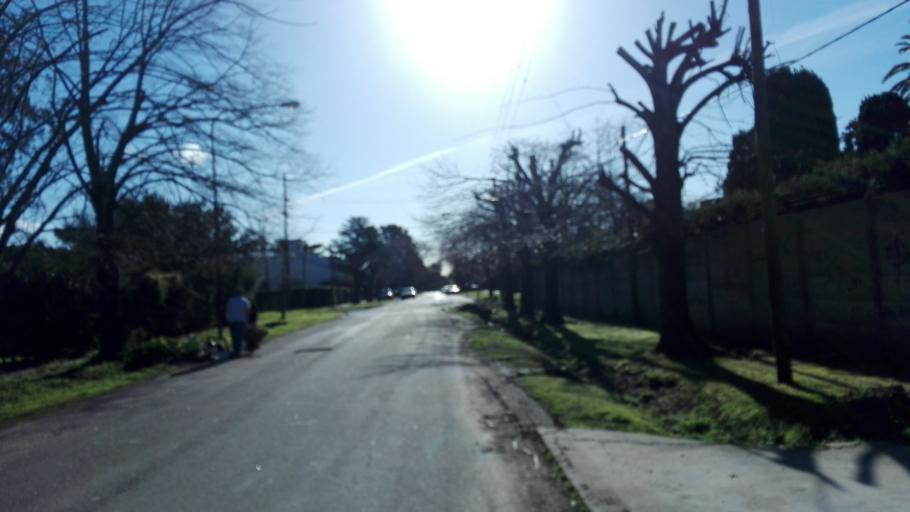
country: AR
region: Buenos Aires
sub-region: Partido de La Plata
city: La Plata
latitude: -34.8794
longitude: -58.0043
